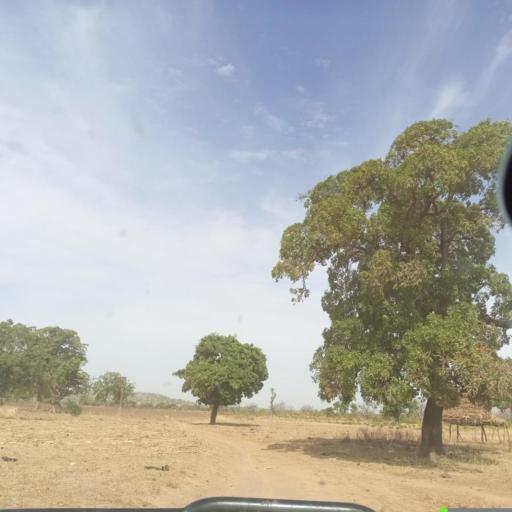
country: ML
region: Koulikoro
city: Koulikoro
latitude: 13.1281
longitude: -7.7088
